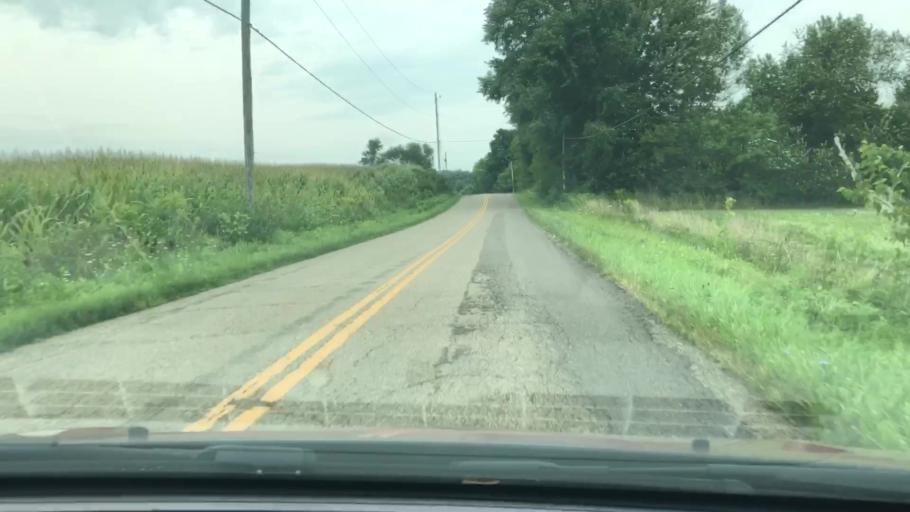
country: US
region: Ohio
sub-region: Knox County
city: Centerburg
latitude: 40.3146
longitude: -82.7260
